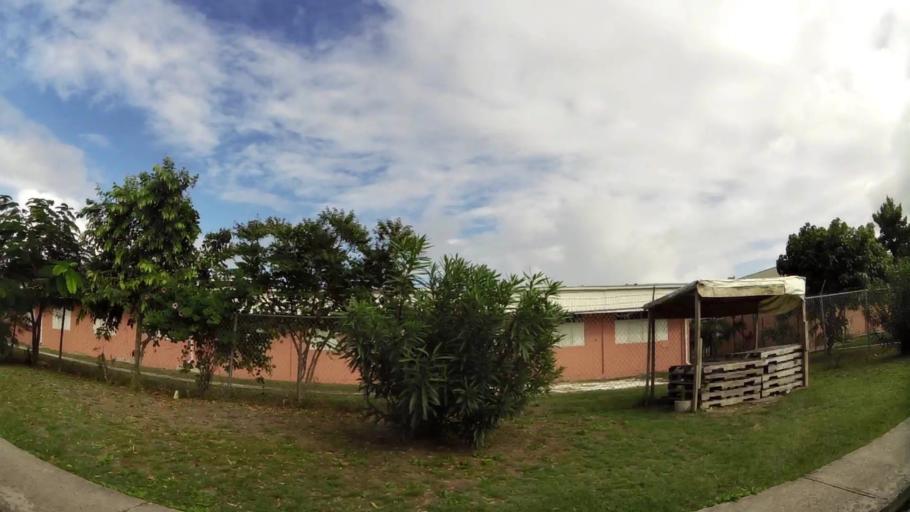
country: AG
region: Saint George
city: Piggotts
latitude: 17.1277
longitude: -61.8227
